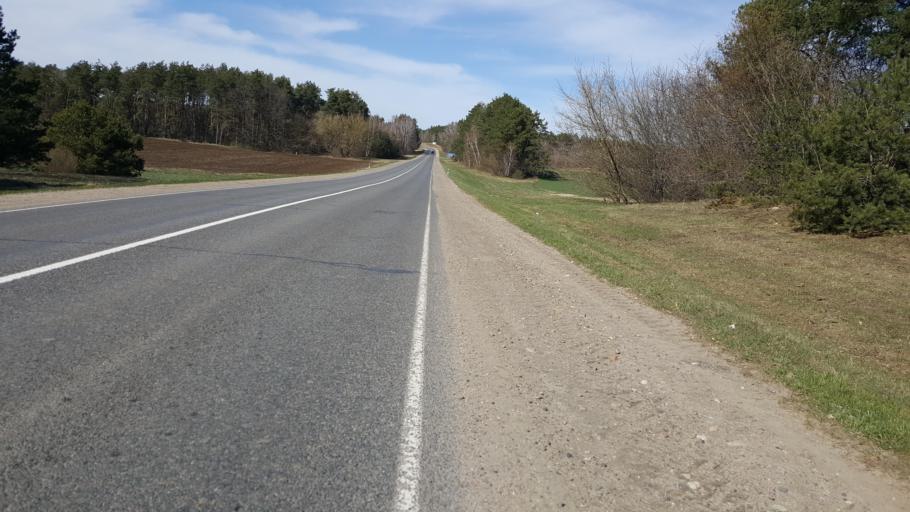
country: BY
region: Brest
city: Kamyanyets
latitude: 52.3379
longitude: 23.7812
